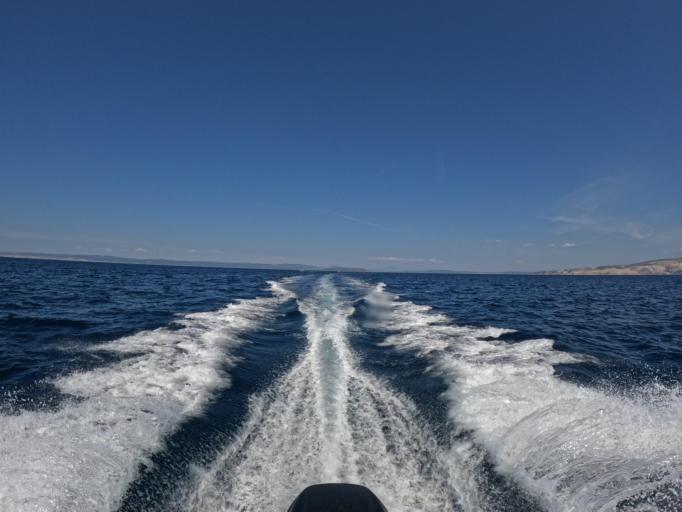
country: HR
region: Primorsko-Goranska
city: Lopar
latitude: 44.8874
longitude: 14.6488
